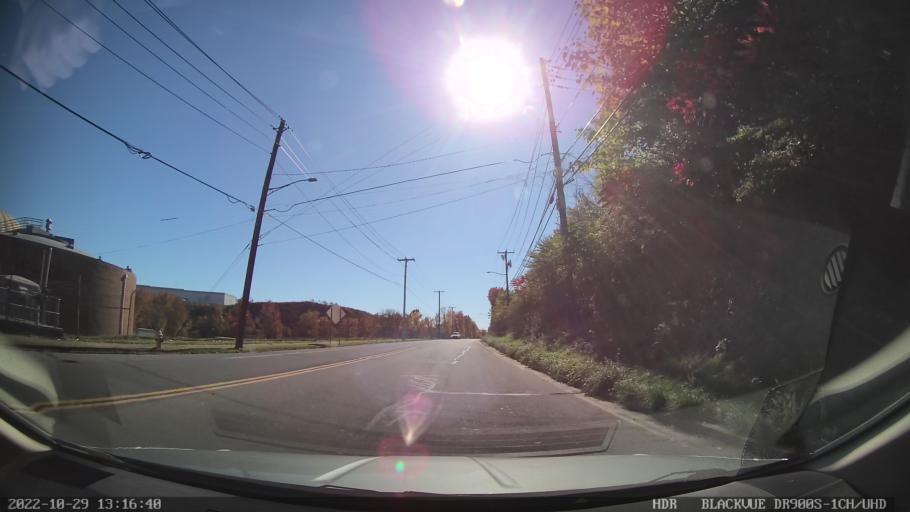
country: US
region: Pennsylvania
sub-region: Northampton County
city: Freemansburg
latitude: 40.6169
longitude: -75.3348
